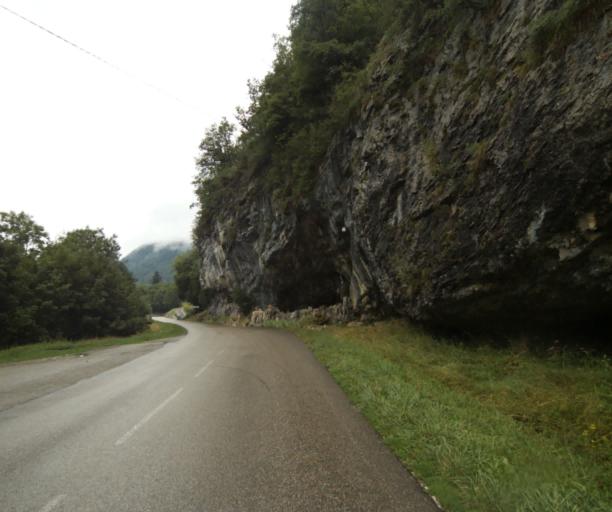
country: FR
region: Rhone-Alpes
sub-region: Departement de la Haute-Savoie
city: Thones
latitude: 45.9008
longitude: 6.2882
